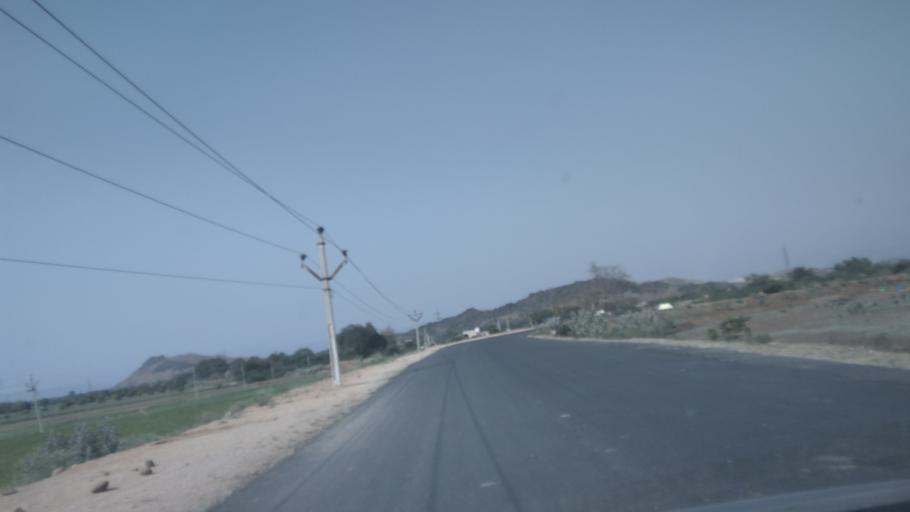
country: IN
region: Andhra Pradesh
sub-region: Chittoor
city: Renigunta
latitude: 13.5381
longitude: 79.4795
